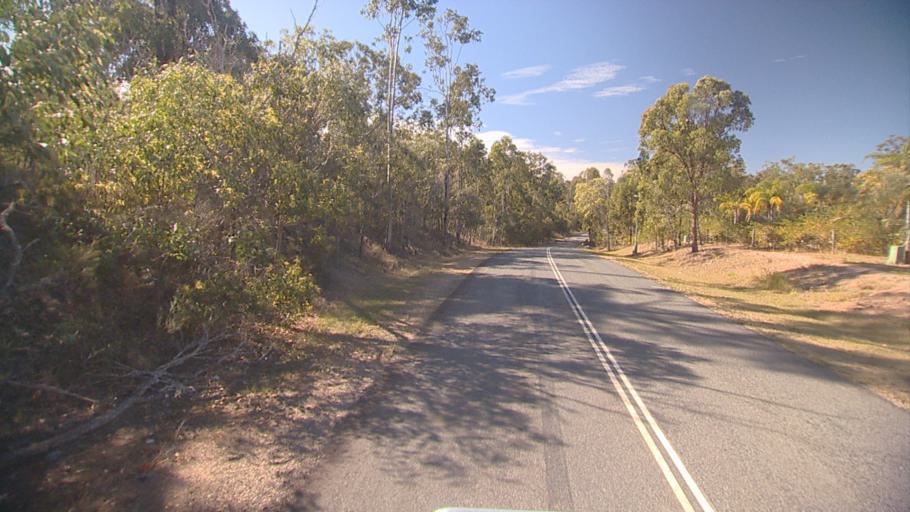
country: AU
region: Queensland
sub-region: Ipswich
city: Springfield Lakes
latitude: -27.7103
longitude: 152.9236
